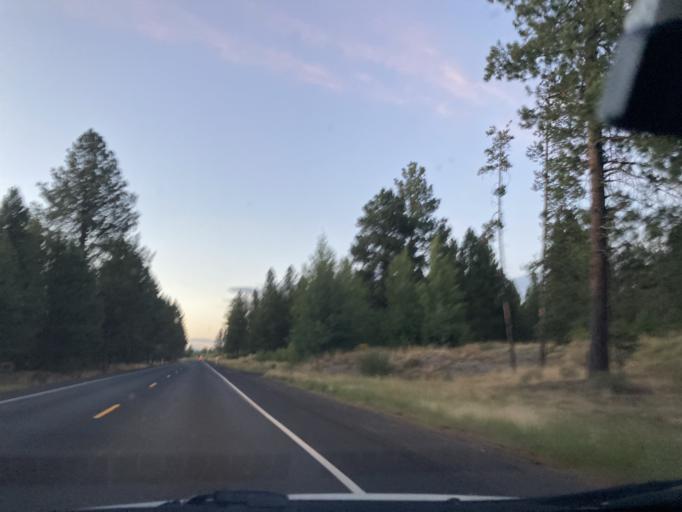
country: US
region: Oregon
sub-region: Deschutes County
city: Three Rivers
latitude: 43.8444
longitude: -121.4414
